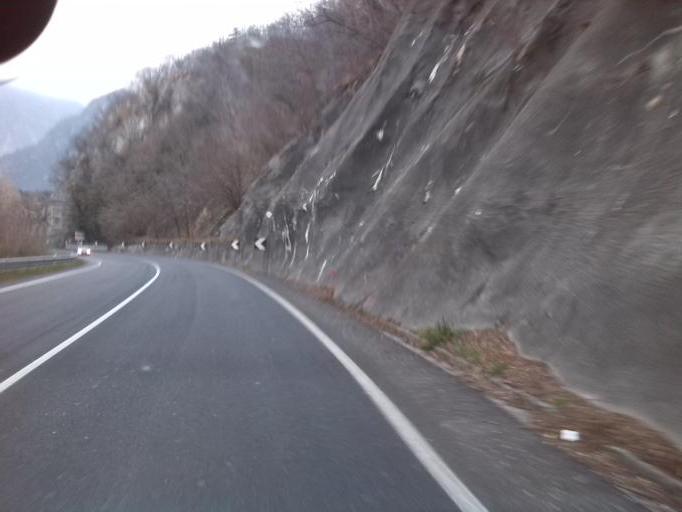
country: IT
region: Friuli Venezia Giulia
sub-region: Provincia di Udine
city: Bordano
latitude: 46.3073
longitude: 13.1271
